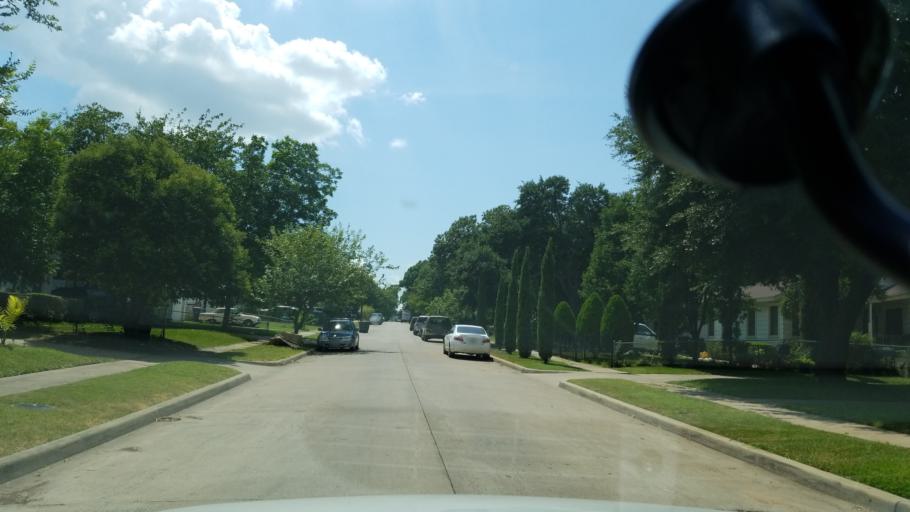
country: US
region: Texas
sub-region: Dallas County
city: Cockrell Hill
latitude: 32.7256
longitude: -96.8781
